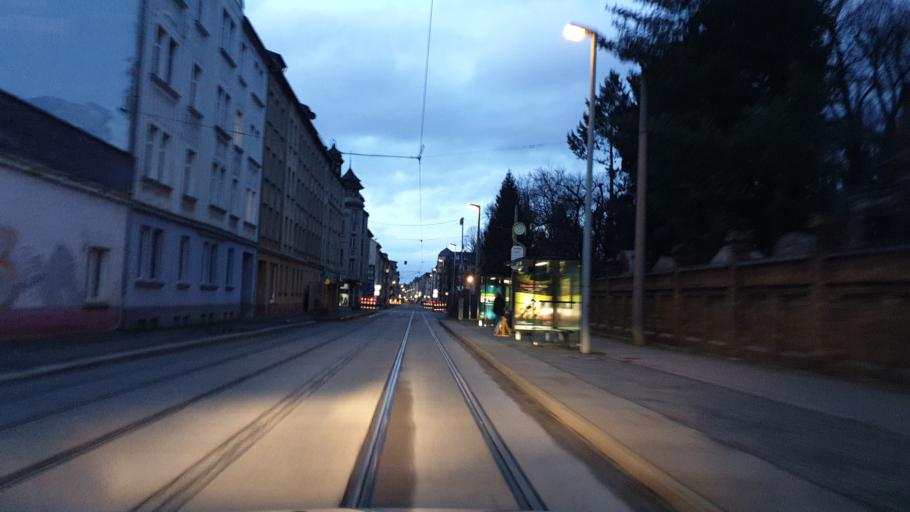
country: DE
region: Thuringia
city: Gera
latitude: 50.8608
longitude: 12.0729
